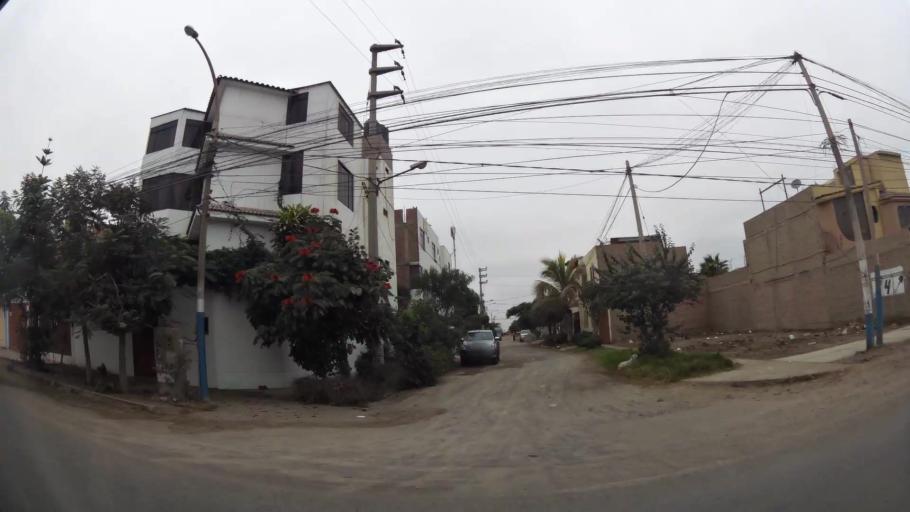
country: PE
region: Ica
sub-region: Provincia de Pisco
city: Pisco
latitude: -13.7169
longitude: -76.2116
